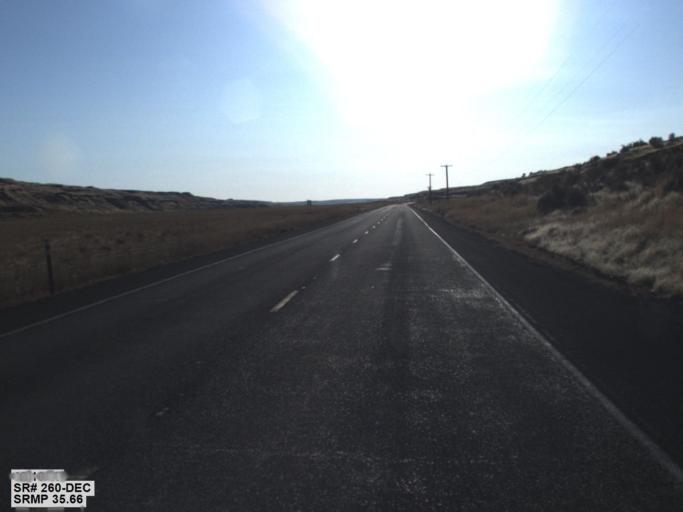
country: US
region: Washington
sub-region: Adams County
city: Ritzville
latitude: 46.7238
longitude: -118.3681
